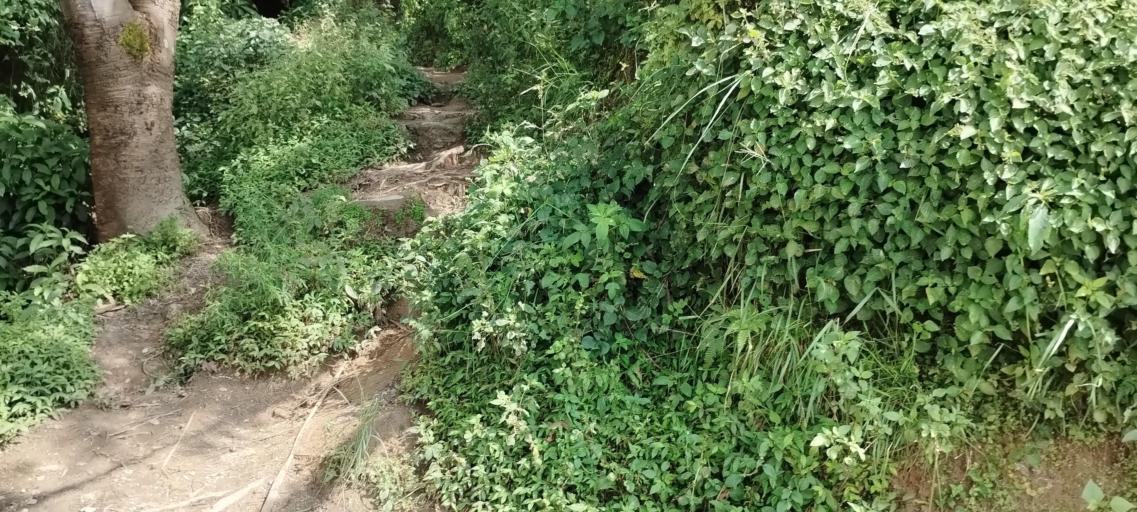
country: NP
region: Central Region
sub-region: Bagmati Zone
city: Kathmandu
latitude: 27.7901
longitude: 85.3613
